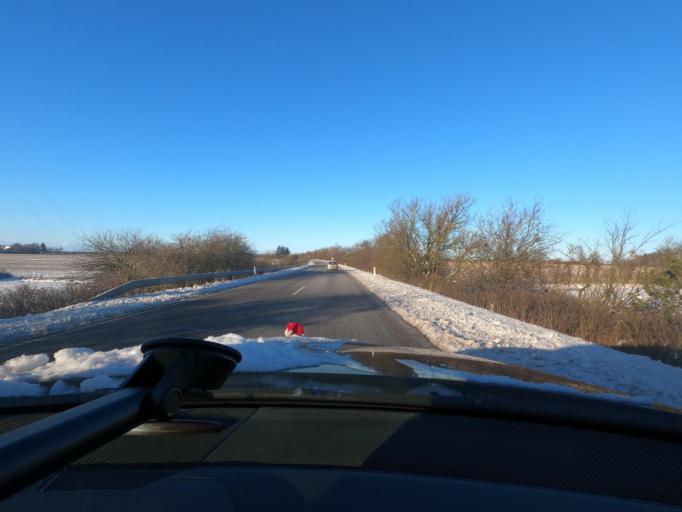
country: DK
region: South Denmark
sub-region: Aabenraa Kommune
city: Rodekro
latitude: 55.1047
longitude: 9.1843
